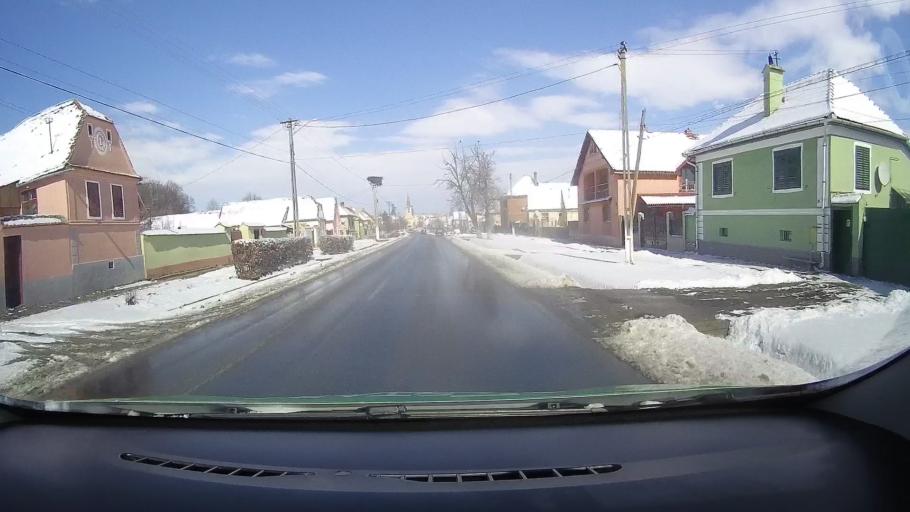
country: RO
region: Sibiu
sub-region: Comuna Nocrich
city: Nocrich
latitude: 45.8905
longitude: 24.4529
